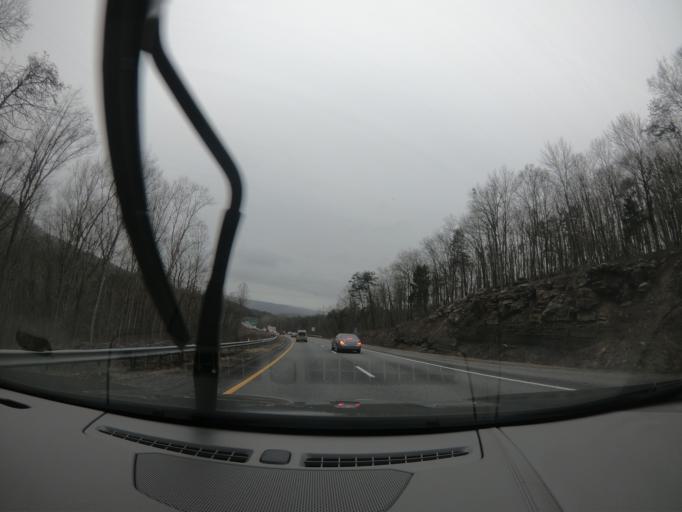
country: US
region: Georgia
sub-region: Walker County
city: Lookout Mountain
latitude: 34.9830
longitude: -85.4665
